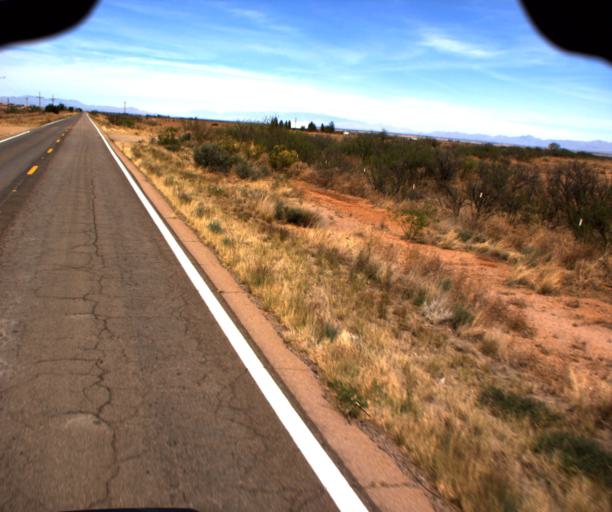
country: US
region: Arizona
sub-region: Cochise County
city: Tombstone
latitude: 31.9239
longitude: -109.8227
